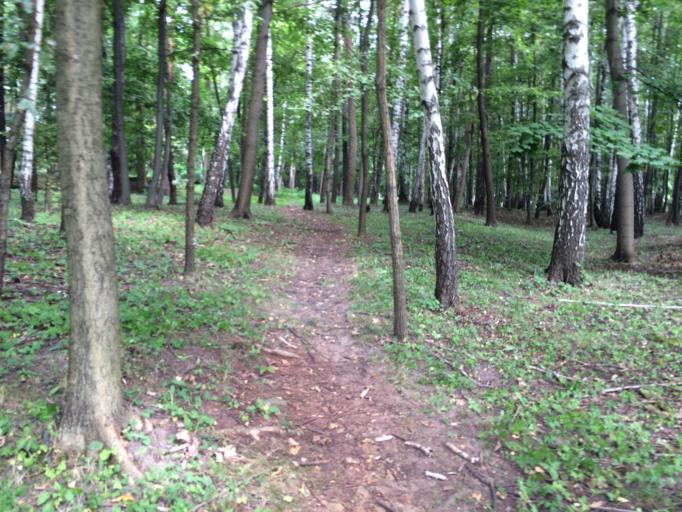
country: PL
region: Swietokrzyskie
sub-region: Powiat starachowicki
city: Starachowice
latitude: 51.0514
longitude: 21.0664
